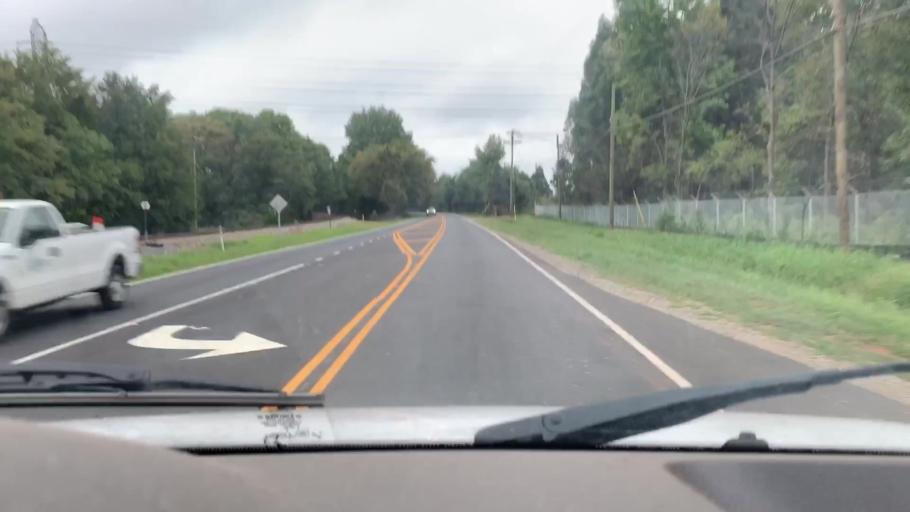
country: US
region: North Carolina
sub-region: Mecklenburg County
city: Huntersville
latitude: 35.3436
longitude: -80.8242
